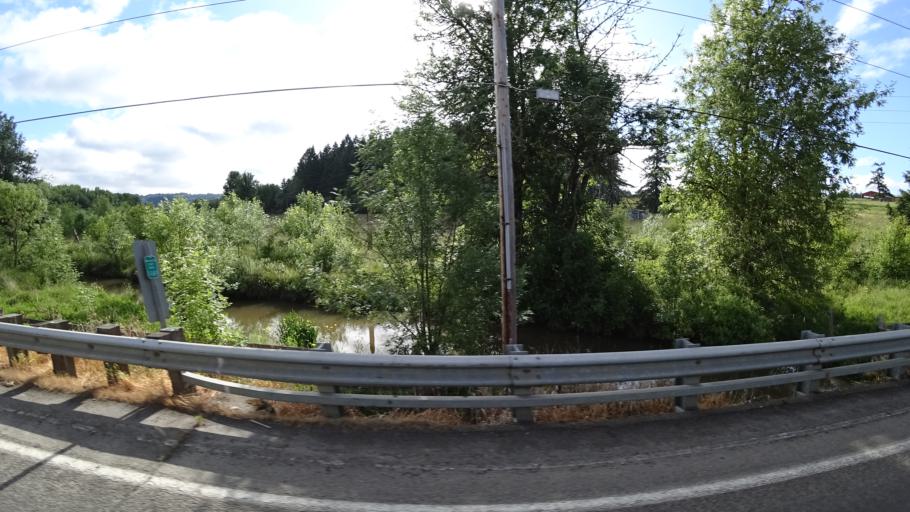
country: US
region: Oregon
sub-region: Washington County
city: Bethany
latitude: 45.5674
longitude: -122.8676
